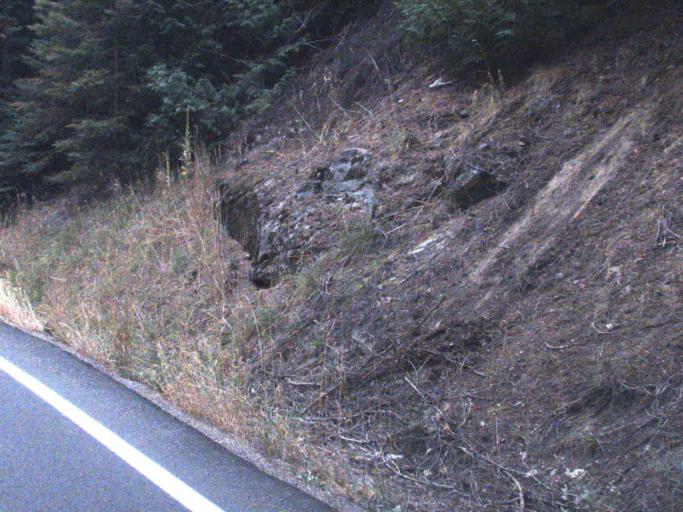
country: US
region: Washington
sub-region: Spokane County
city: Otis Orchards-East Farms
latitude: 47.8780
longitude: -117.1483
